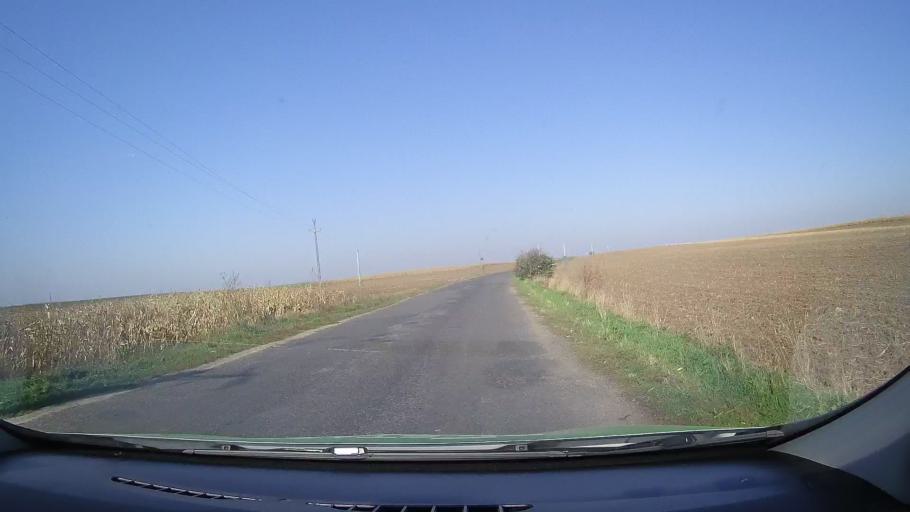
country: RO
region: Satu Mare
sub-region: Comuna Petresti
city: Petresti
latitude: 47.6105
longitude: 22.3539
